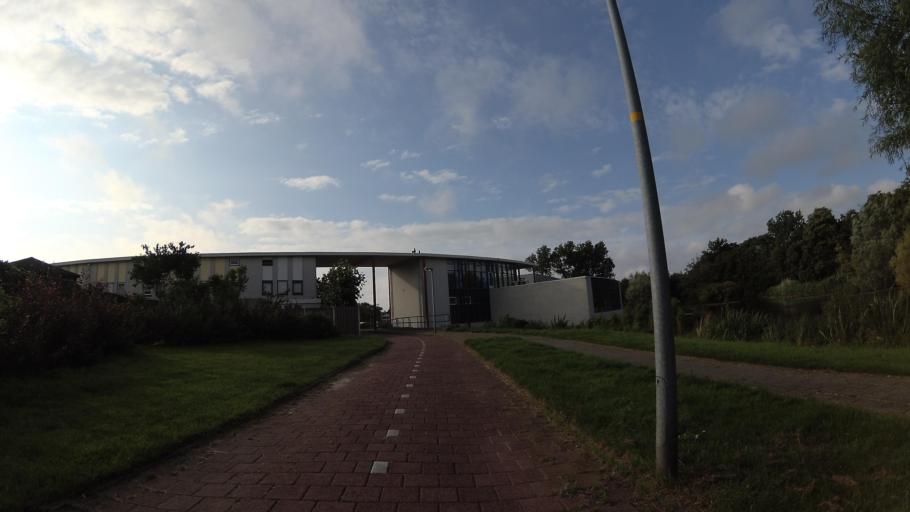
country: NL
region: North Holland
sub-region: Gemeente Den Helder
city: Den Helder
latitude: 52.8944
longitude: 4.7479
